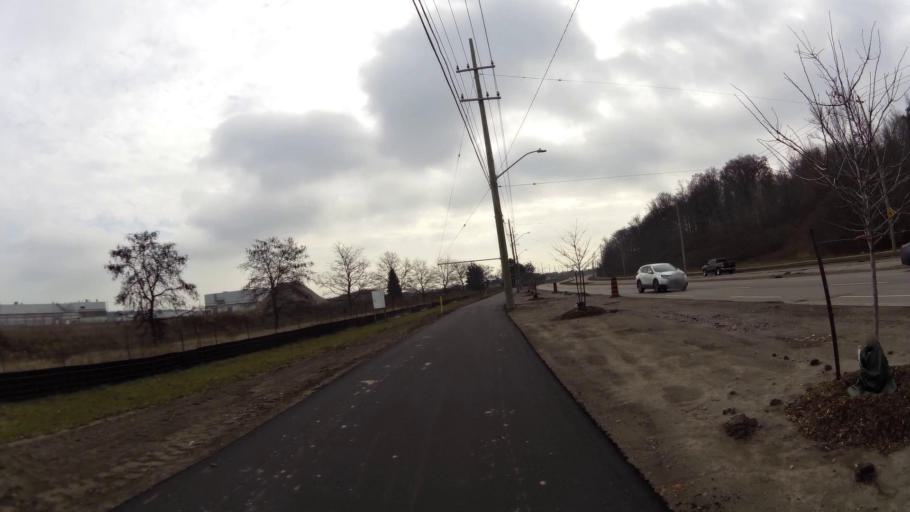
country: CA
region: Ontario
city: Kitchener
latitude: 43.4091
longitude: -80.4599
